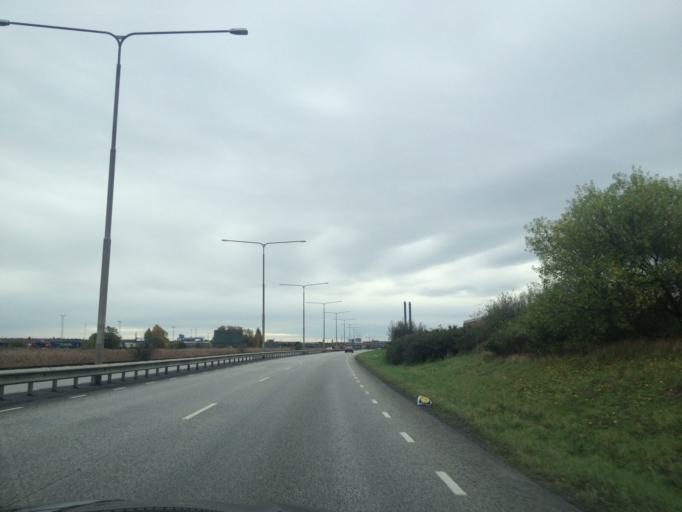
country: SE
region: Skane
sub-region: Burlovs Kommun
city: Arloev
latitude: 55.6251
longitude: 13.0502
